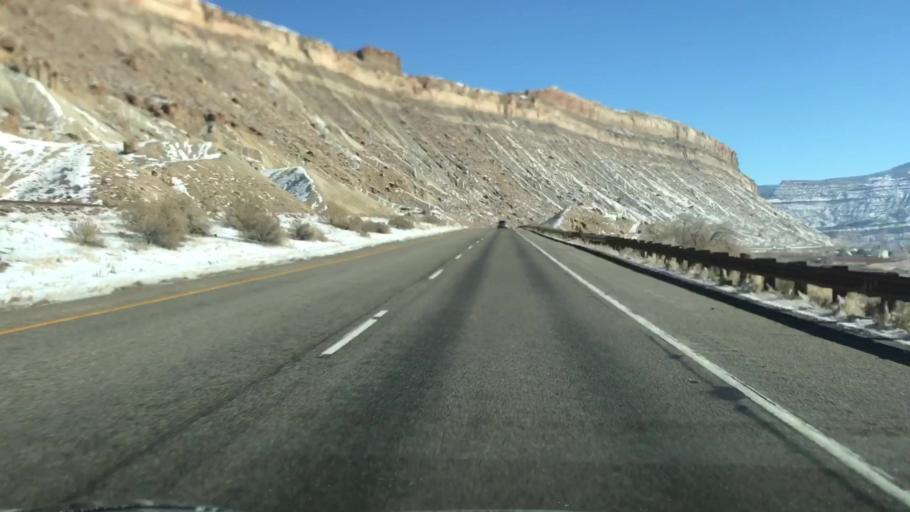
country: US
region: Colorado
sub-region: Mesa County
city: Palisade
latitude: 39.1192
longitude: -108.3811
